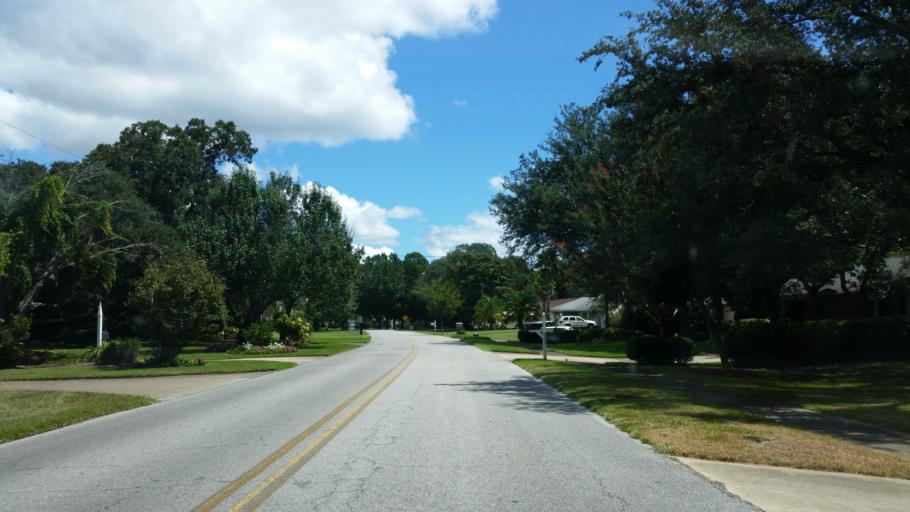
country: US
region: Florida
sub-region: Okaloosa County
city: Ocean City
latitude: 30.4219
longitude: -86.6008
